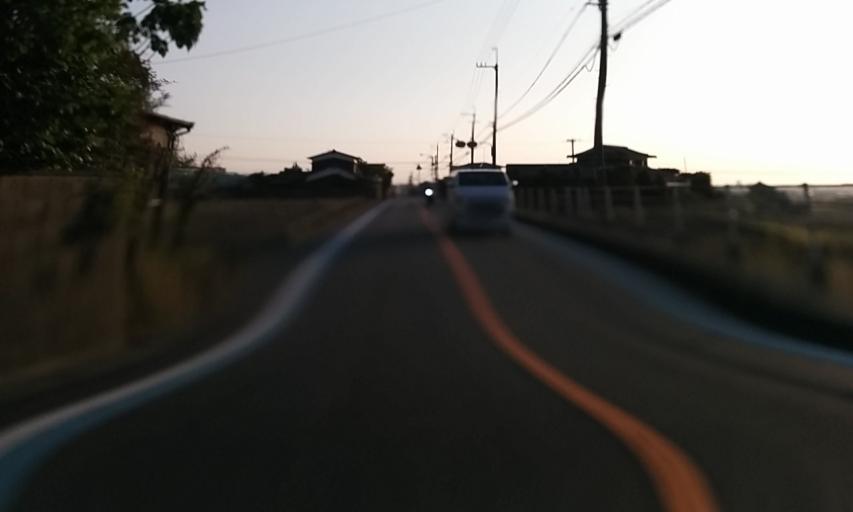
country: JP
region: Ehime
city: Masaki-cho
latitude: 33.7776
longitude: 132.7543
